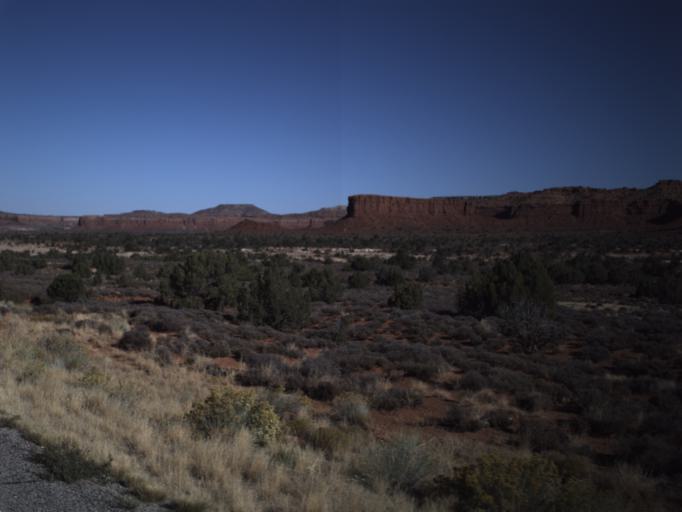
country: US
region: Utah
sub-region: San Juan County
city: Blanding
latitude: 37.6733
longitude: -110.2053
